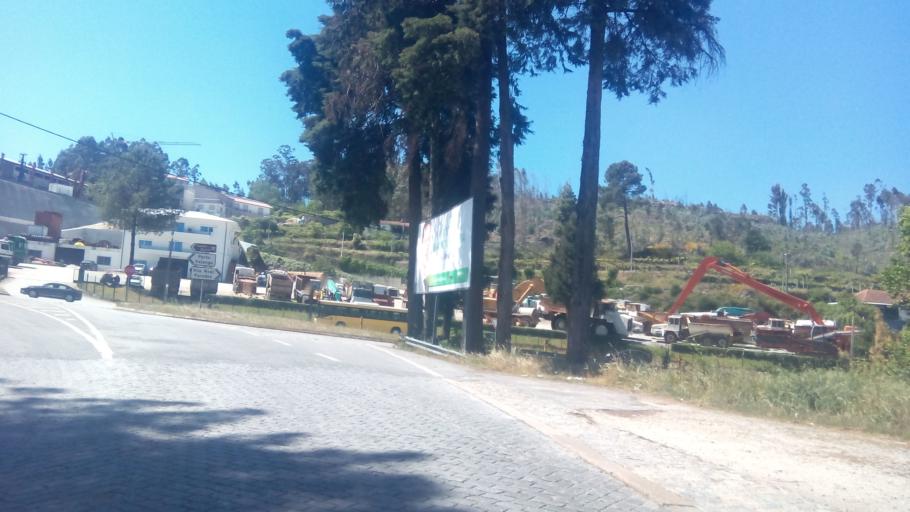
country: PT
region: Porto
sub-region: Paredes
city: Baltar
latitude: 41.1940
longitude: -8.3646
